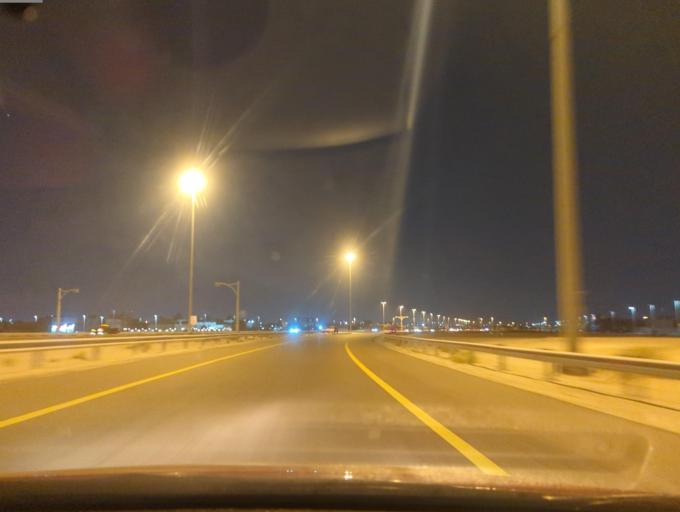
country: AE
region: Abu Dhabi
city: Abu Dhabi
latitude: 24.3804
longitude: 54.7289
